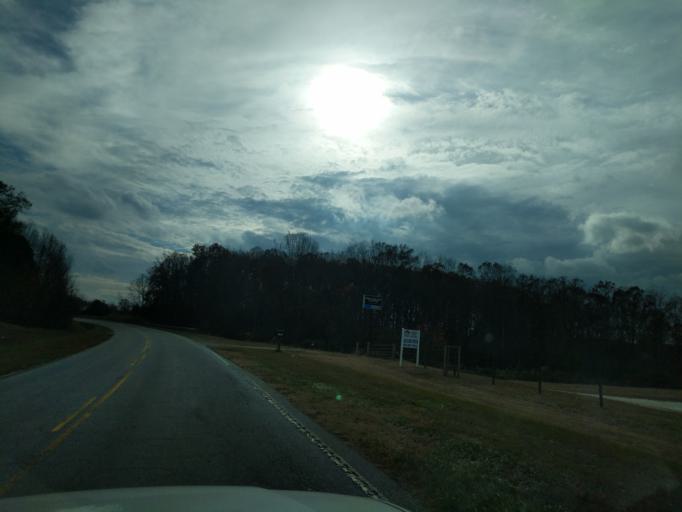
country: US
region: Georgia
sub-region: Franklin County
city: Gumlog
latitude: 34.5604
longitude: -83.0515
